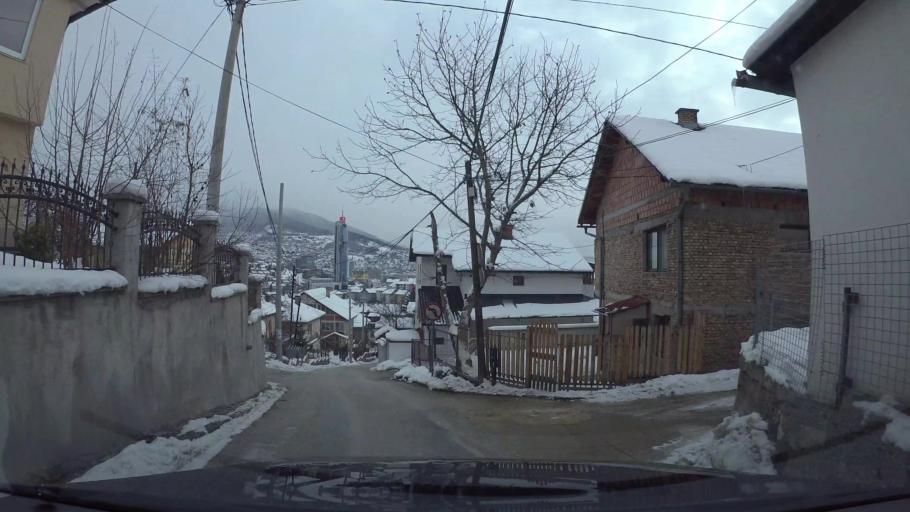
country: BA
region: Federation of Bosnia and Herzegovina
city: Kobilja Glava
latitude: 43.8675
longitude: 18.3973
